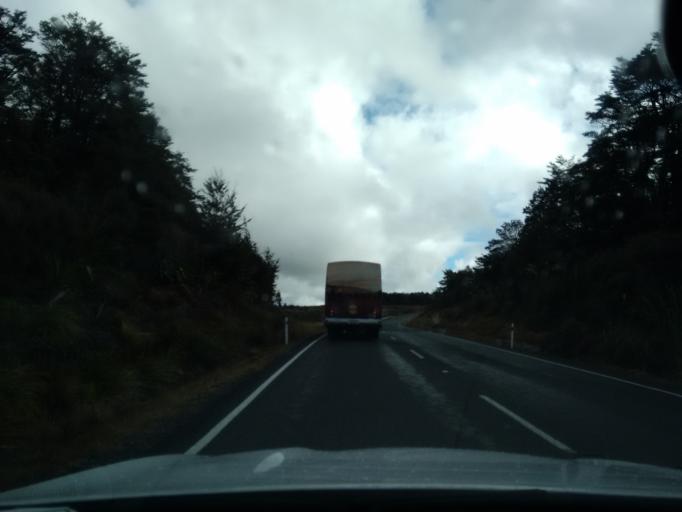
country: NZ
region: Manawatu-Wanganui
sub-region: Ruapehu District
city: Waiouru
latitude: -39.1771
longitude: 175.4694
